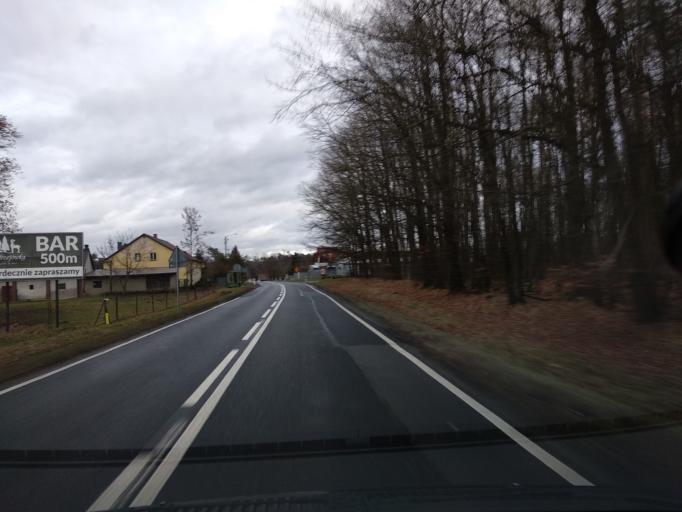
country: PL
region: Lower Silesian Voivodeship
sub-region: Powiat olesnicki
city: Olesnica
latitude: 51.2456
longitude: 17.4717
